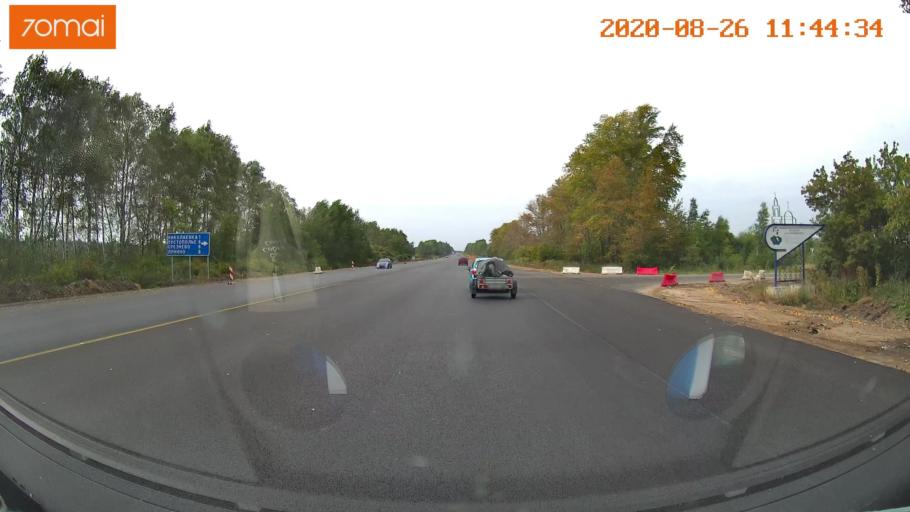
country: RU
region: Rjazan
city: Lesnoy
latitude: 54.2989
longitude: 40.6498
